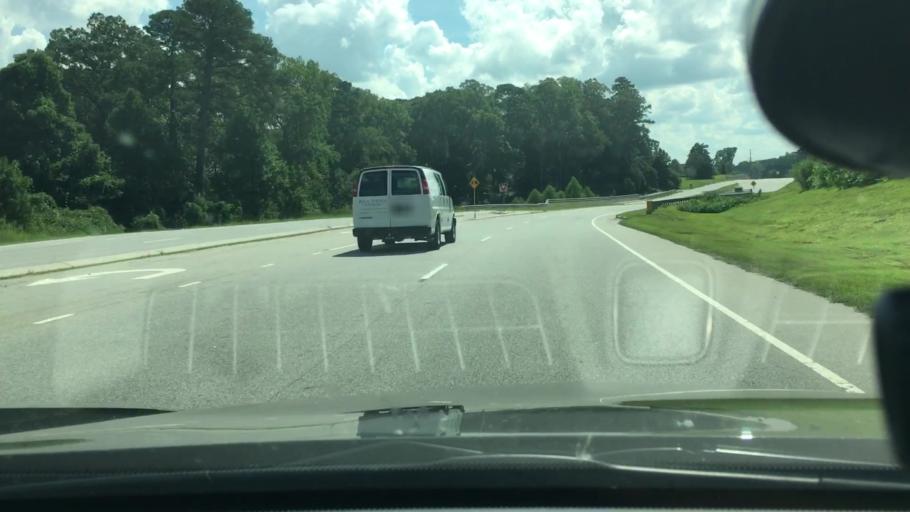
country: US
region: North Carolina
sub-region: Pitt County
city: Greenville
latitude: 35.6241
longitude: -77.4206
